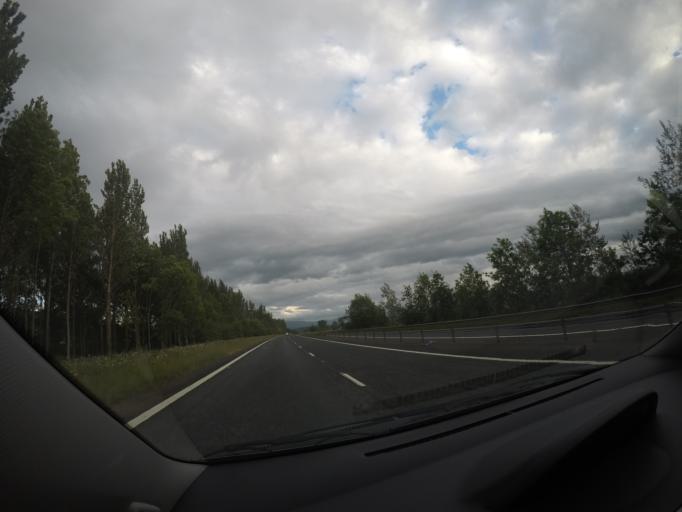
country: GB
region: England
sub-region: Cumbria
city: Appleby-in-Westmorland
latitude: 54.5763
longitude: -2.4692
